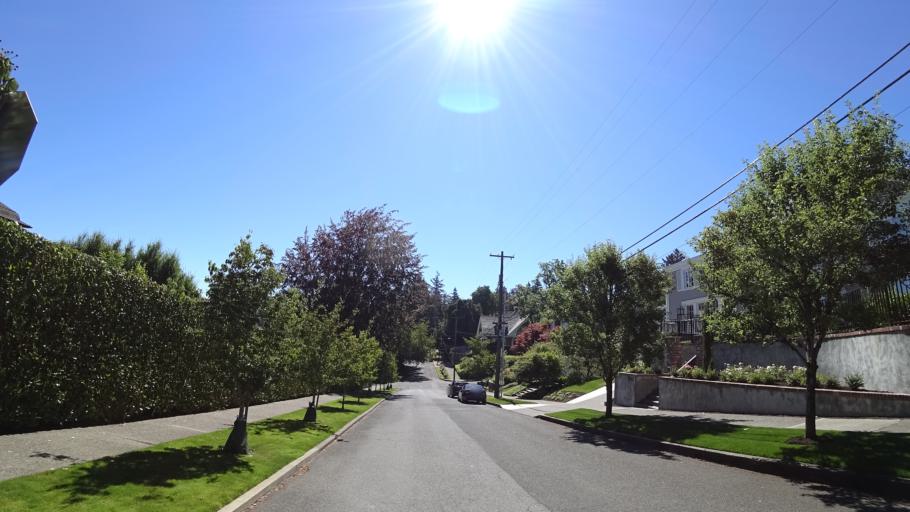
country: US
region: Oregon
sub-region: Multnomah County
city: Portland
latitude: 45.5095
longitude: -122.6969
